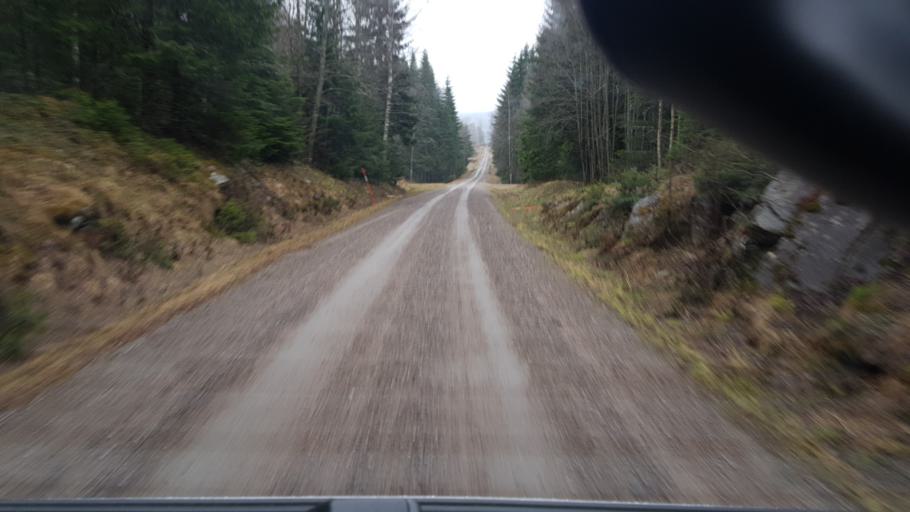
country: SE
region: Vaermland
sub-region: Eda Kommun
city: Charlottenberg
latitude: 59.9933
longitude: 12.5070
